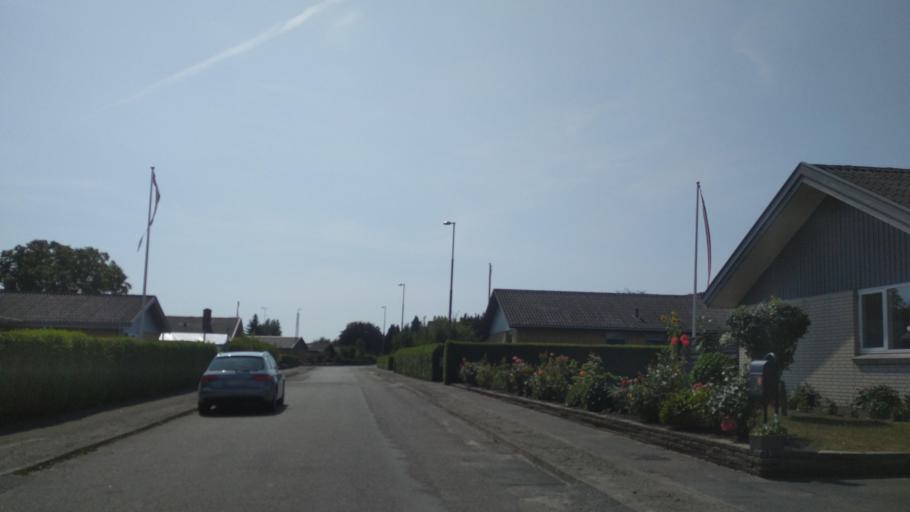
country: DK
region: Capital Region
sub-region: Bornholm Kommune
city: Akirkeby
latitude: 55.0690
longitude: 14.9284
